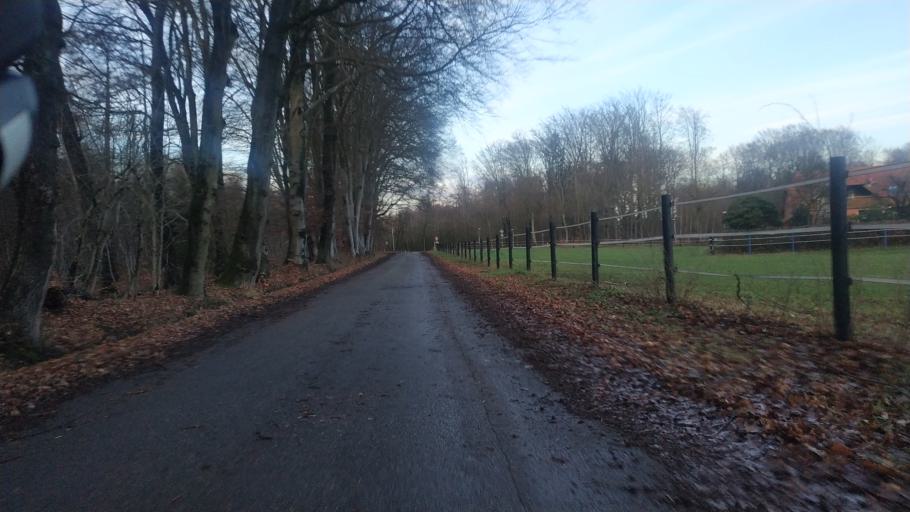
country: DE
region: North Rhine-Westphalia
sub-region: Regierungsbezirk Munster
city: Mettingen
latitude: 52.3003
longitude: 7.7670
